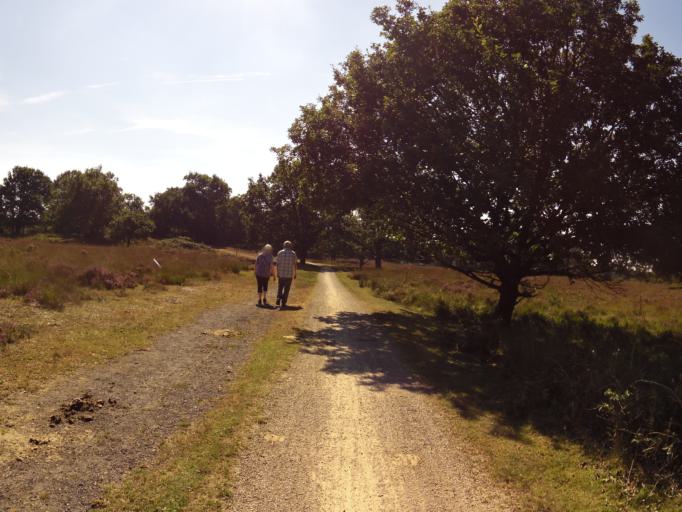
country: NL
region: Overijssel
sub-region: Gemeente Haaksbergen
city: Haaksbergen
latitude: 52.1569
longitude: 6.7981
